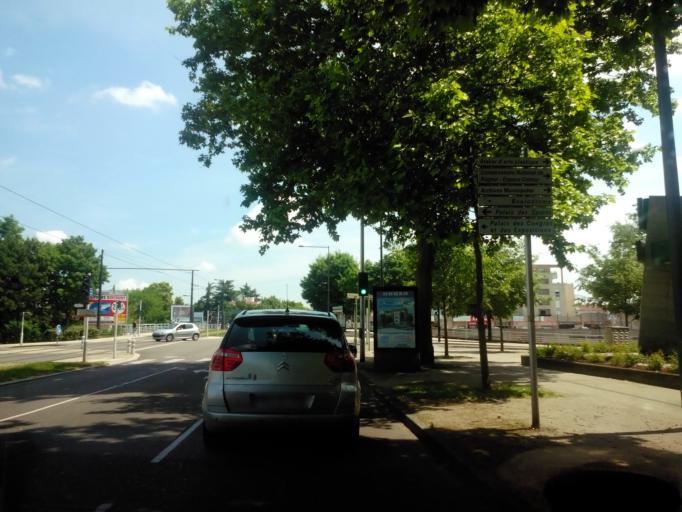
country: FR
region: Bourgogne
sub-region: Departement de la Cote-d'Or
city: Saint-Apollinaire
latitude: 47.3287
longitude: 5.0552
